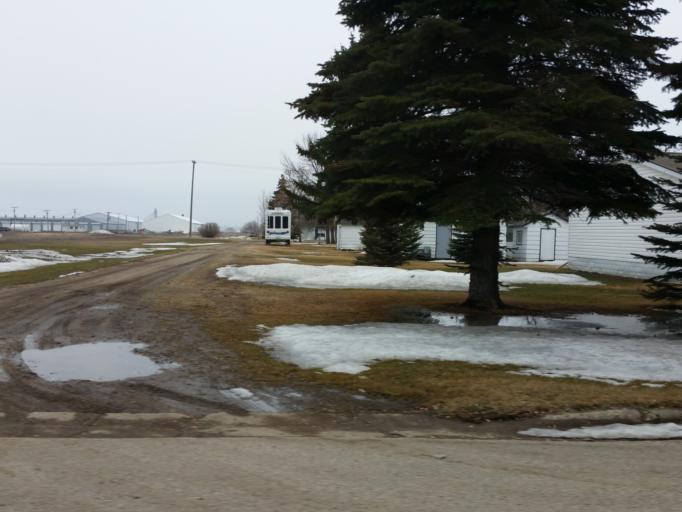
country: US
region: North Dakota
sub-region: Walsh County
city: Grafton
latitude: 48.6171
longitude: -97.4474
